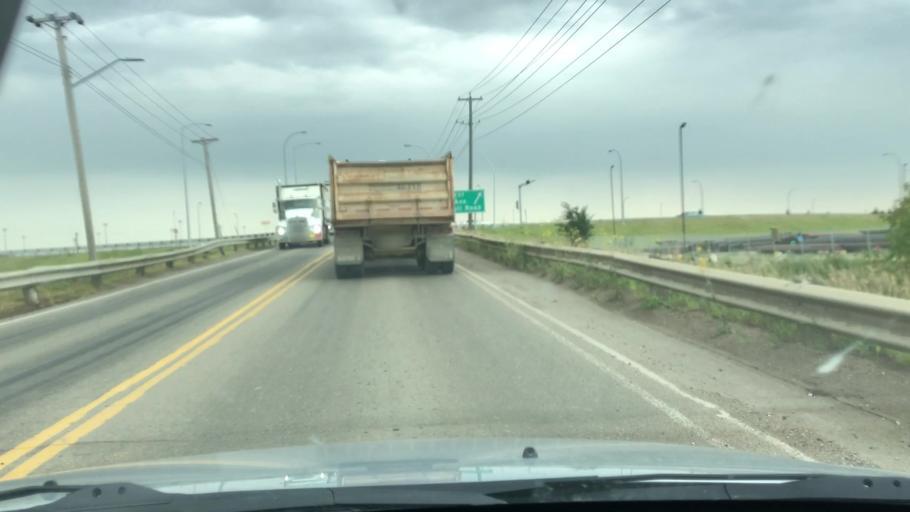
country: CA
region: Alberta
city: Sherwood Park
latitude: 53.5188
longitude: -113.3939
